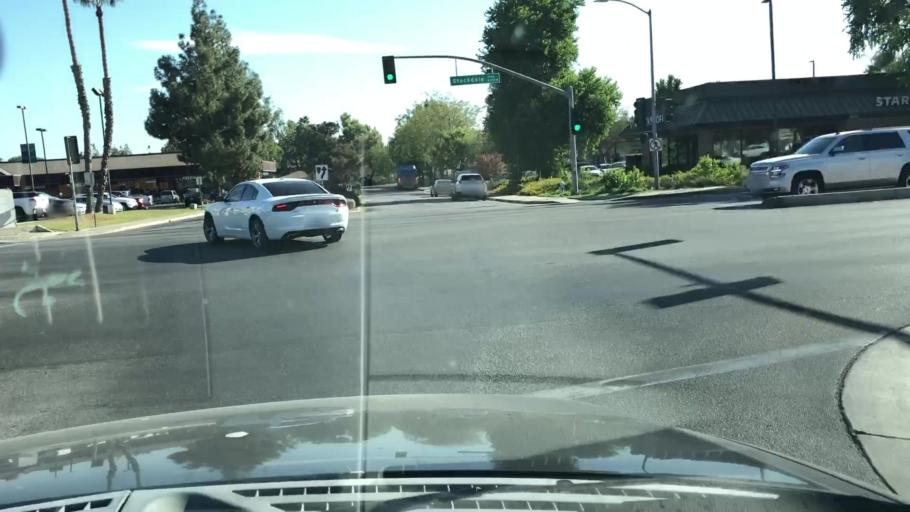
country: US
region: California
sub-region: Kern County
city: Bakersfield
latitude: 35.3544
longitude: -119.0576
